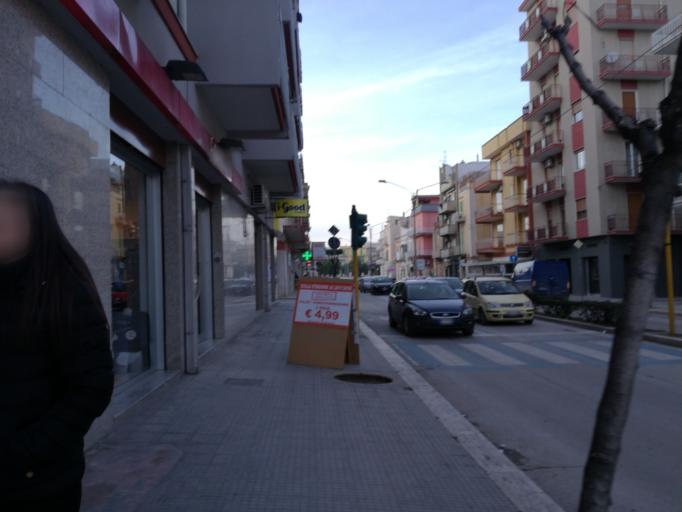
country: IT
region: Apulia
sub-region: Provincia di Bari
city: Corato
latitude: 41.1504
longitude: 16.4083
